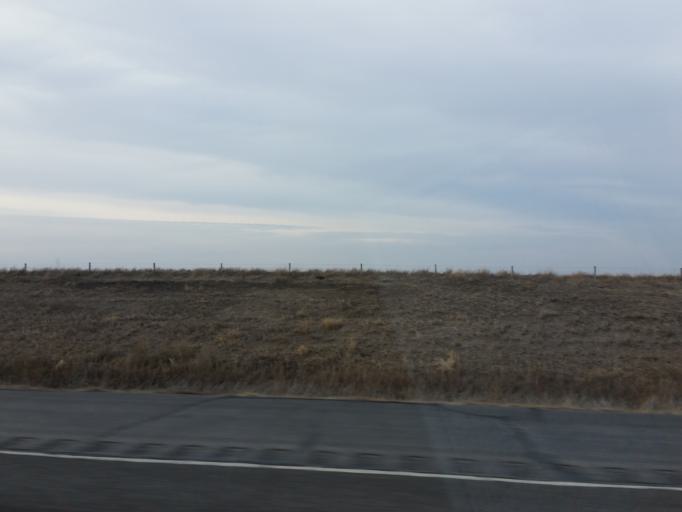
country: US
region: North Dakota
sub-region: Cass County
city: Casselton
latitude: 46.8768
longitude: -97.1292
